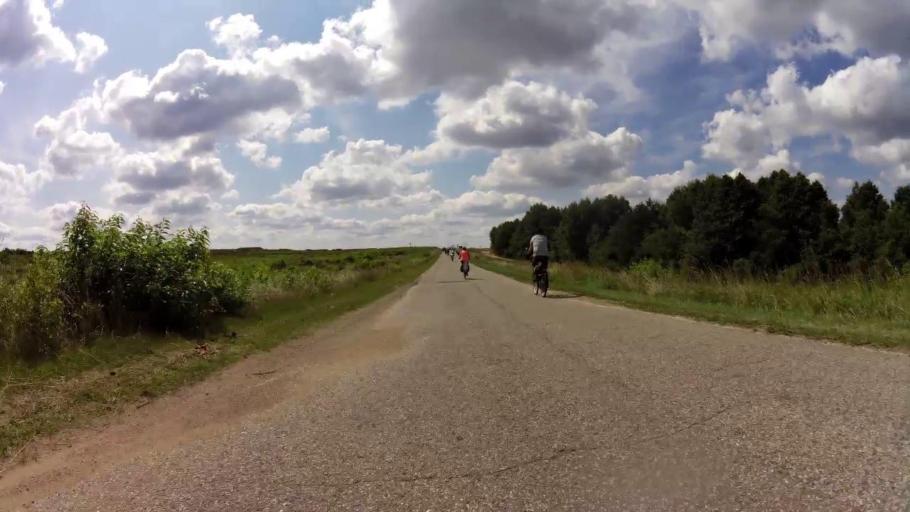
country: PL
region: West Pomeranian Voivodeship
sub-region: Powiat drawski
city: Drawsko Pomorskie
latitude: 53.4463
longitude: 15.7627
